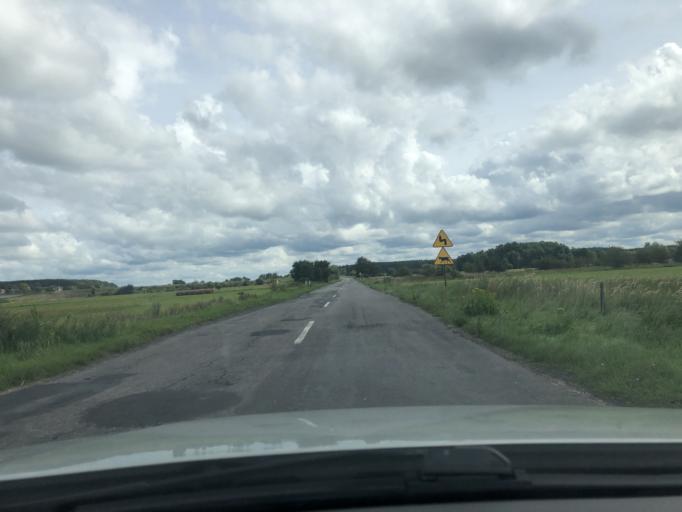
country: PL
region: Lubusz
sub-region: Powiat strzelecko-drezdenecki
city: Drezdenko
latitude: 52.8422
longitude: 15.9089
